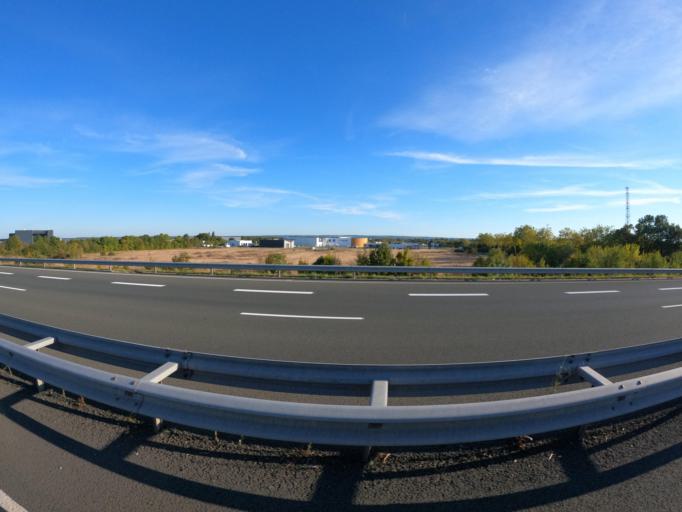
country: FR
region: Pays de la Loire
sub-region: Departement de Maine-et-Loire
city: Chemille-Melay
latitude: 47.2410
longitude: -0.7258
